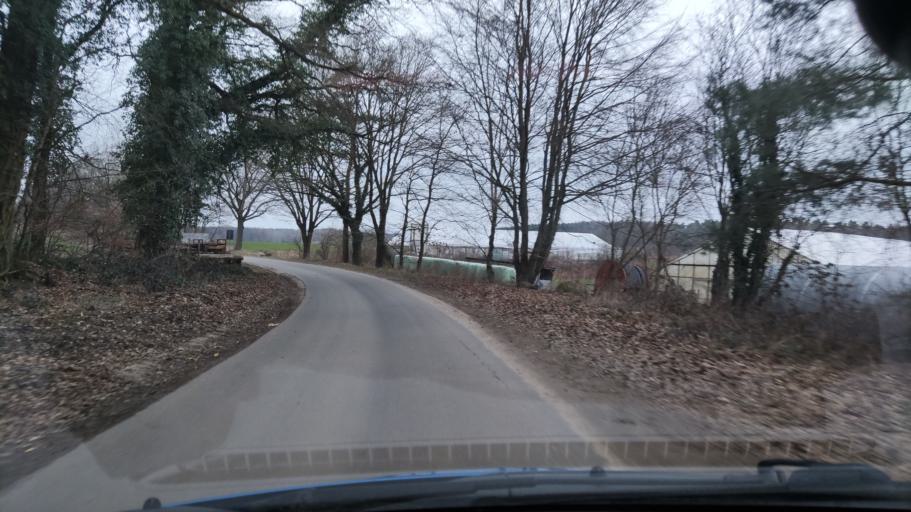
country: DE
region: Lower Saxony
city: Betzendorf
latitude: 53.1243
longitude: 10.3236
